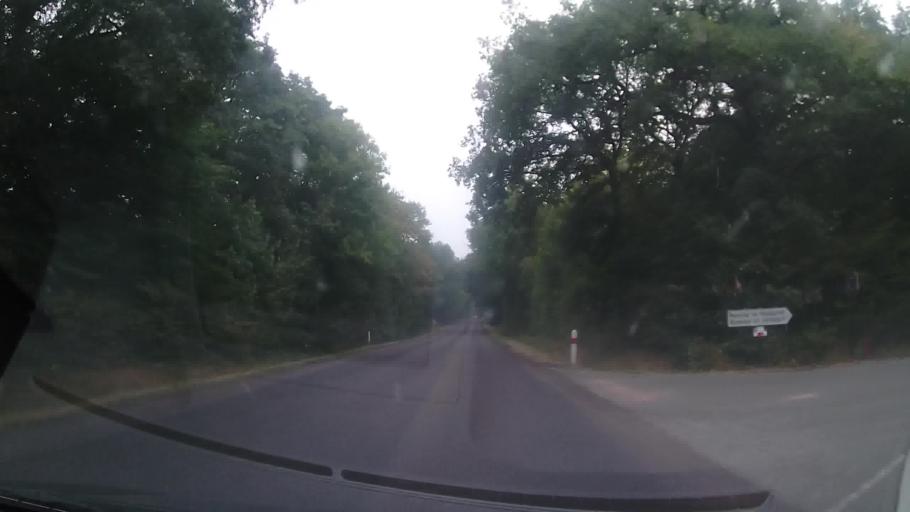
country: FR
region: Ile-de-France
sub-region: Departement de l'Essonne
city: Dourdan
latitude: 48.5432
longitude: 1.9954
